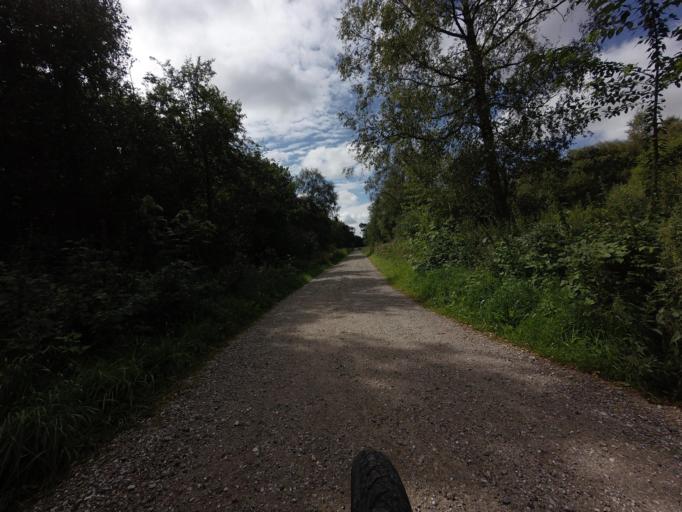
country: DK
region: Central Jutland
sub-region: Norddjurs Kommune
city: Auning
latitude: 56.4411
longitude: 10.3671
